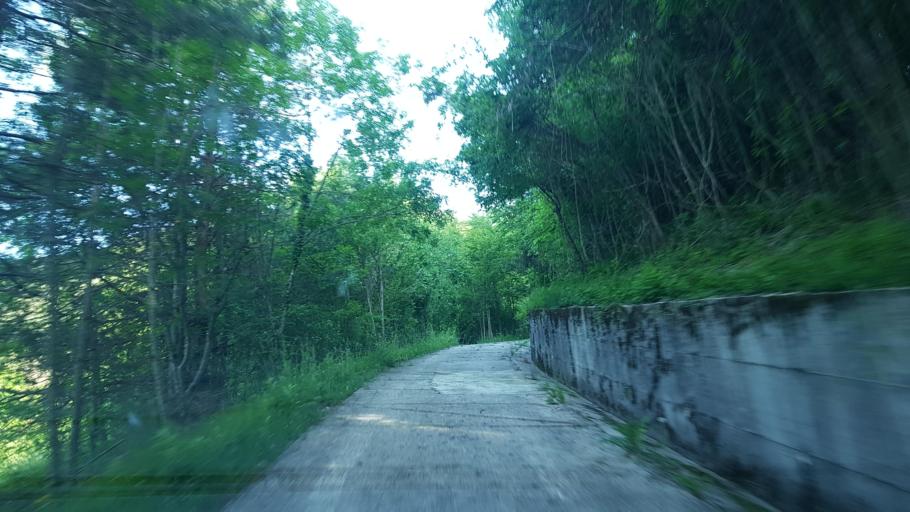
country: IT
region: Friuli Venezia Giulia
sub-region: Provincia di Udine
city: Moggio di Sotto
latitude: 46.4112
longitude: 13.1869
